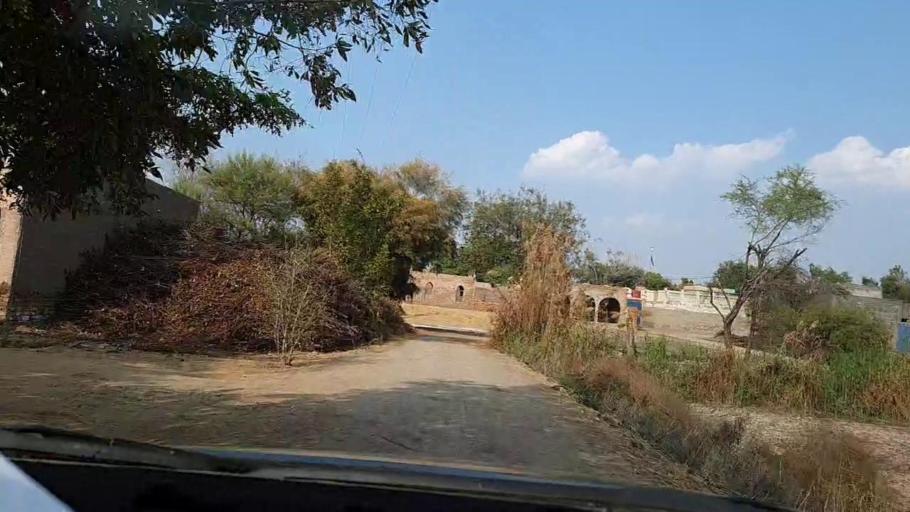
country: PK
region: Sindh
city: Nawabshah
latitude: 26.1687
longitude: 68.3642
